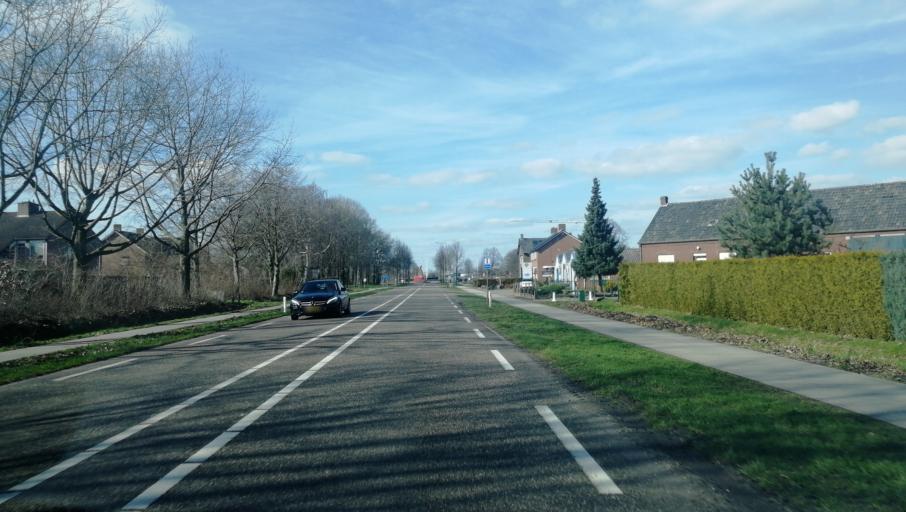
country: NL
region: Limburg
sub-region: Gemeente Peel en Maas
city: Maasbree
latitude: 51.4126
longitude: 6.0469
